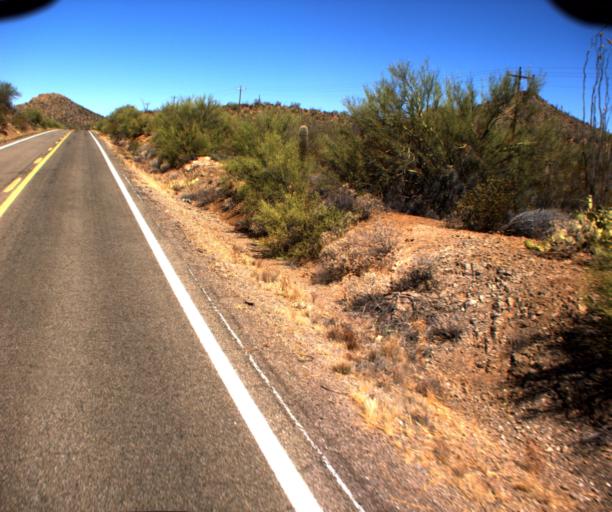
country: US
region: Arizona
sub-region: Pima County
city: Sells
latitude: 32.1697
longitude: -112.1430
